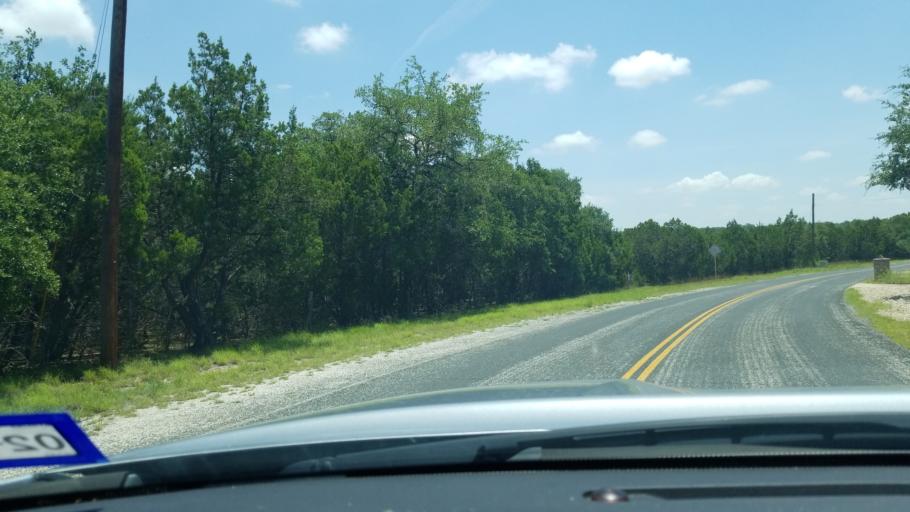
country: US
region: Texas
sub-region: Bexar County
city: Timberwood Park
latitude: 29.7055
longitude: -98.5088
